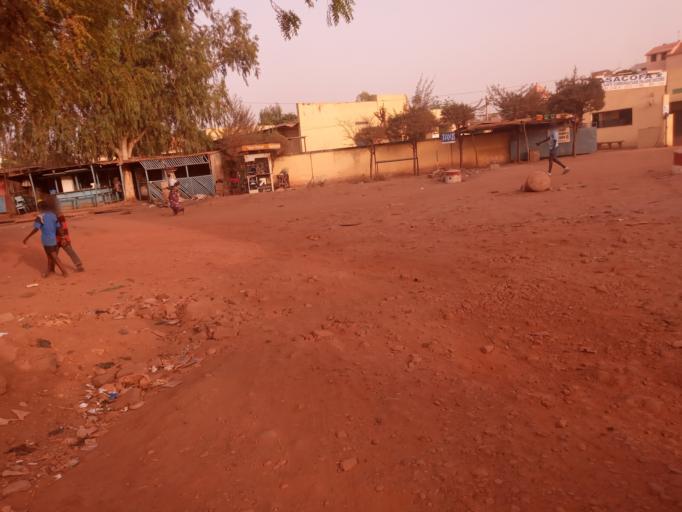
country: ML
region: Bamako
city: Bamako
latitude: 12.5928
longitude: -7.9587
